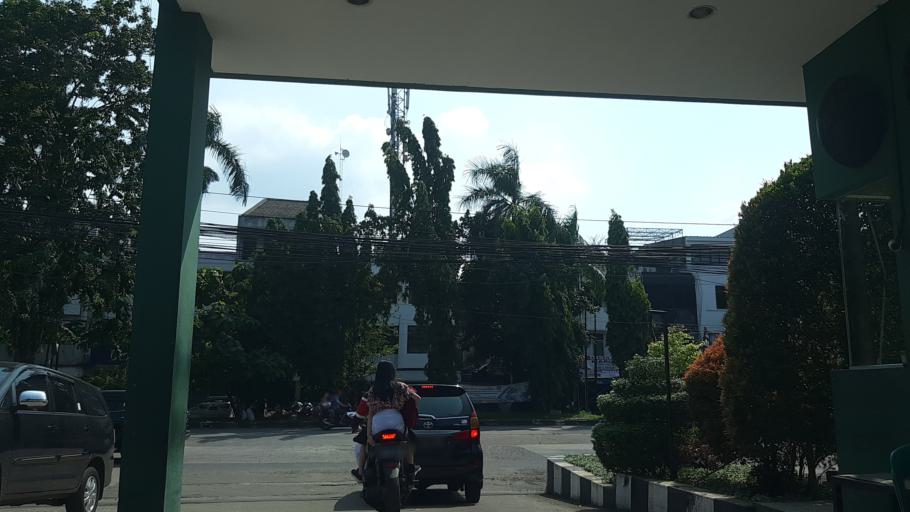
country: ID
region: Jakarta Raya
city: Jakarta
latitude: -6.1708
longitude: 106.7760
